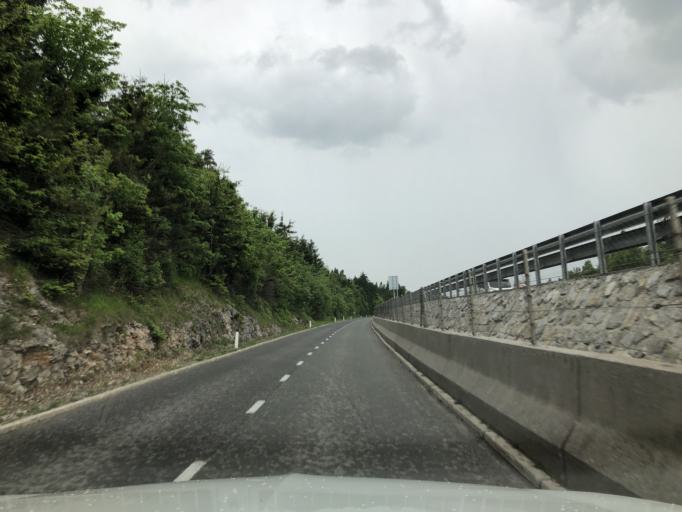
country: SI
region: Postojna
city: Postojna
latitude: 45.7995
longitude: 14.2597
